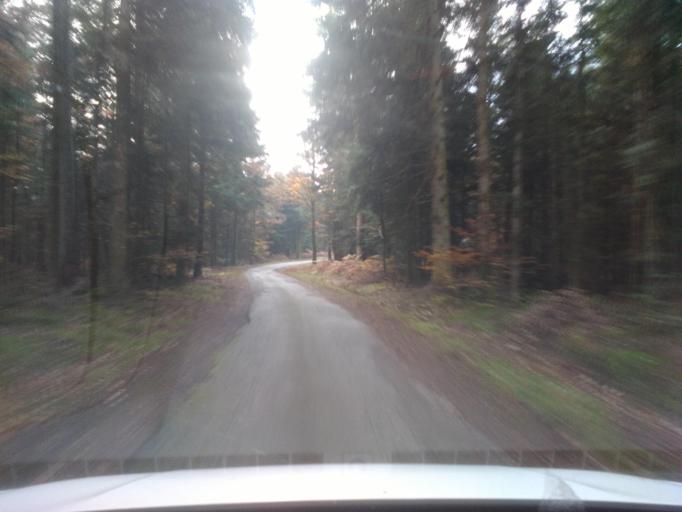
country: FR
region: Lorraine
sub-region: Departement des Vosges
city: Moyenmoutier
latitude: 48.3581
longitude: 6.9038
